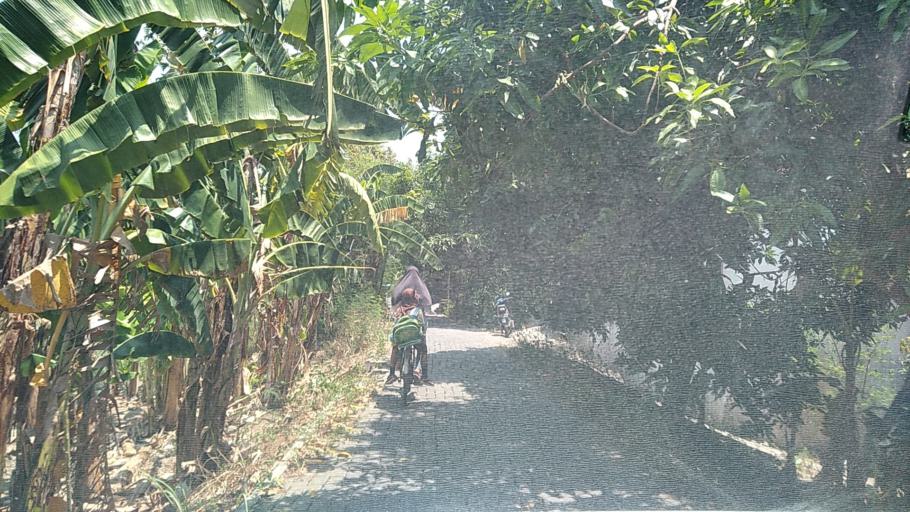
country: ID
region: Central Java
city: Mranggen
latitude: -6.9729
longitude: 110.4974
